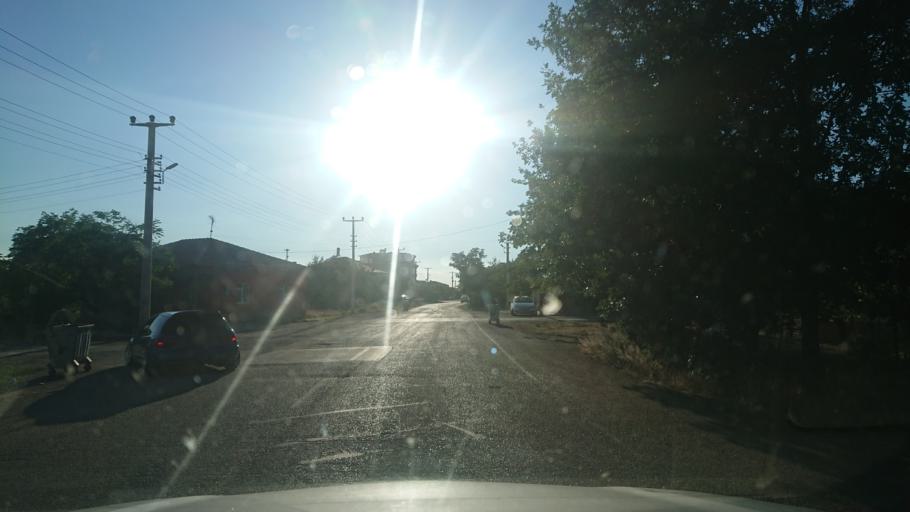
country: TR
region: Aksaray
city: Aksaray
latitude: 38.3889
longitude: 33.9993
